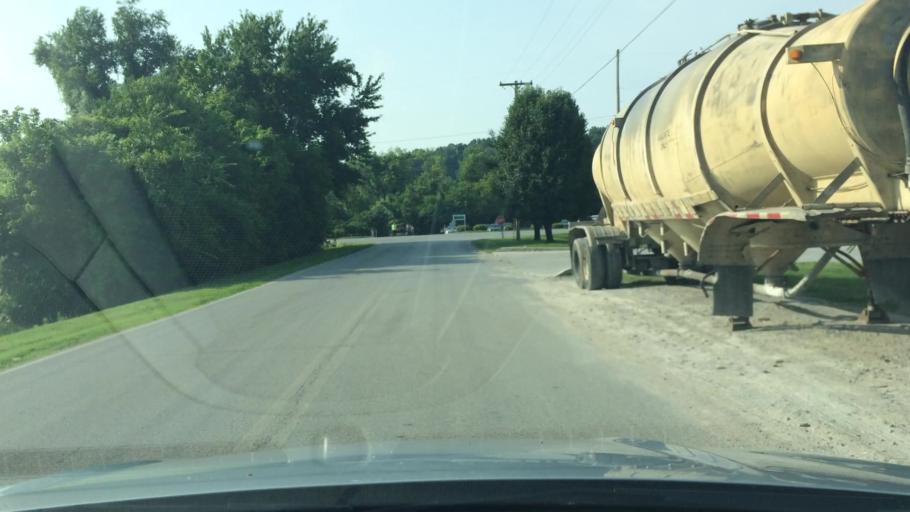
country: US
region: Tennessee
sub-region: Loudon County
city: Lenoir City
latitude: 35.7851
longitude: -84.2656
